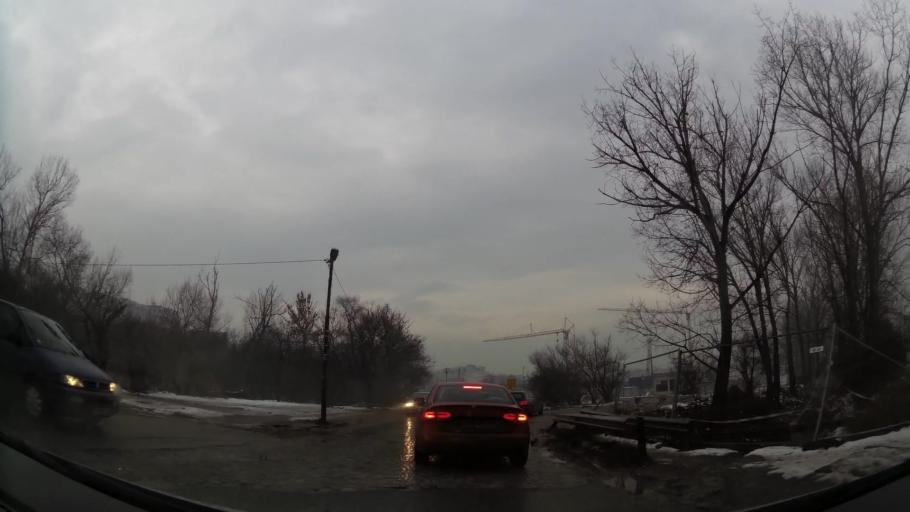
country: BG
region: Sofia-Capital
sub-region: Stolichna Obshtina
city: Sofia
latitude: 42.6826
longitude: 23.2556
